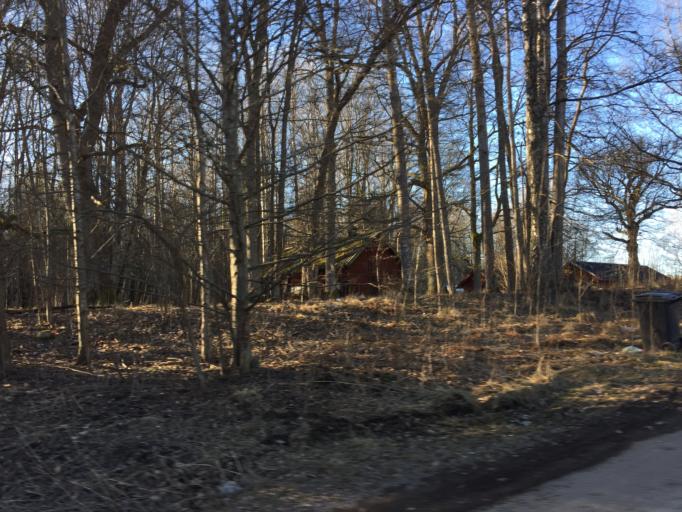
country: SE
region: Soedermanland
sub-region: Vingakers Kommun
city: Vingaker
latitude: 59.0307
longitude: 15.6794
